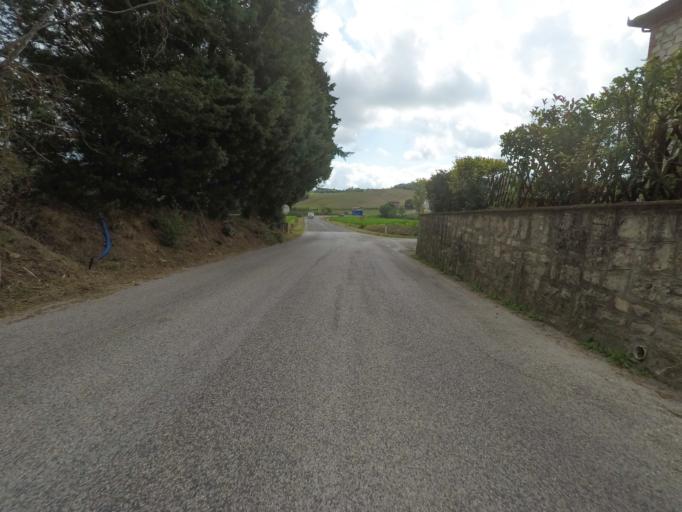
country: IT
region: Tuscany
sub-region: Provincia di Siena
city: Torrita di Siena
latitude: 43.1616
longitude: 11.7715
